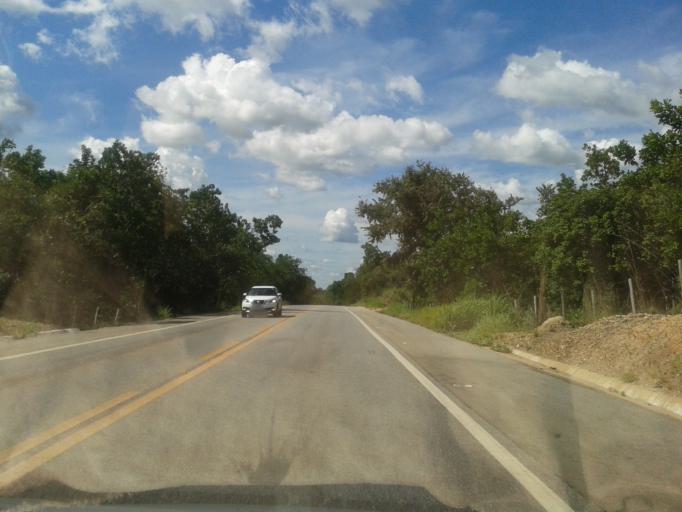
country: BR
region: Goias
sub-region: Itapuranga
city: Itapuranga
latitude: -15.5611
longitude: -50.2819
